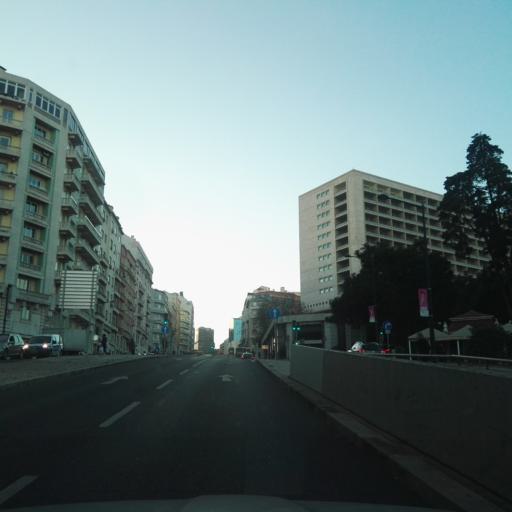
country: PT
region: Lisbon
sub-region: Lisbon
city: Lisbon
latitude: 38.7252
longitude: -9.1529
